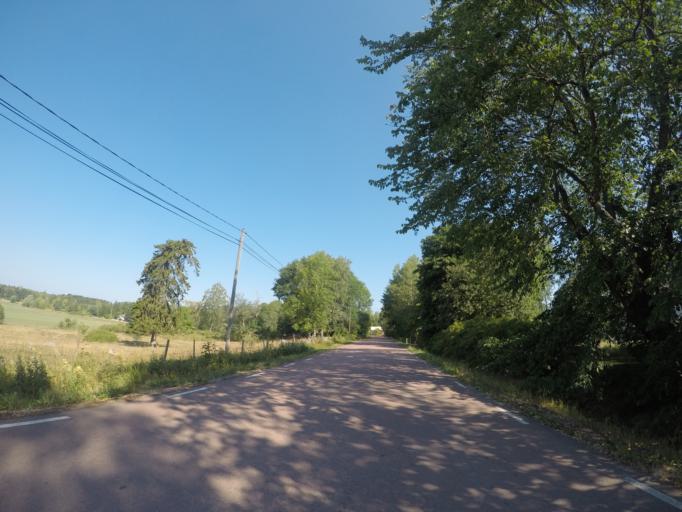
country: AX
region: Alands landsbygd
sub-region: Jomala
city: Jomala
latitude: 60.2097
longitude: 19.9737
